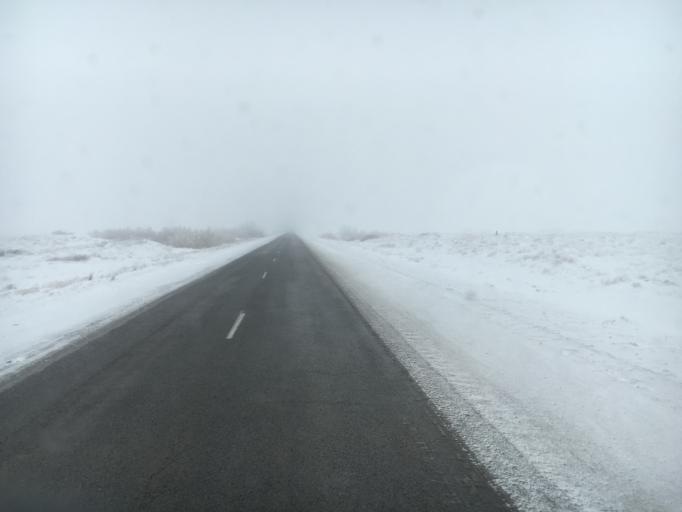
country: KZ
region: Batys Qazaqstan
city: Dzhambeyty
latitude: 50.1853
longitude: 53.3680
